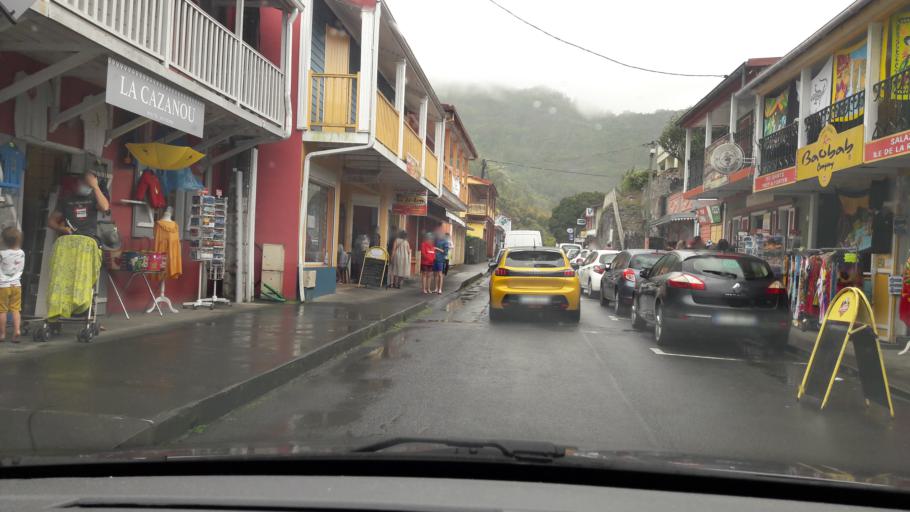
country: RE
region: Reunion
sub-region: Reunion
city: Salazie
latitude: -21.0652
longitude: 55.5197
